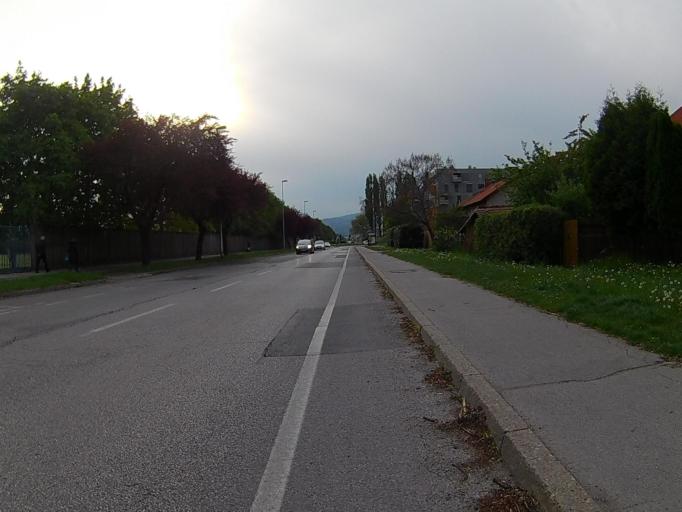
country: SI
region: Maribor
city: Maribor
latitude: 46.5506
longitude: 15.6338
